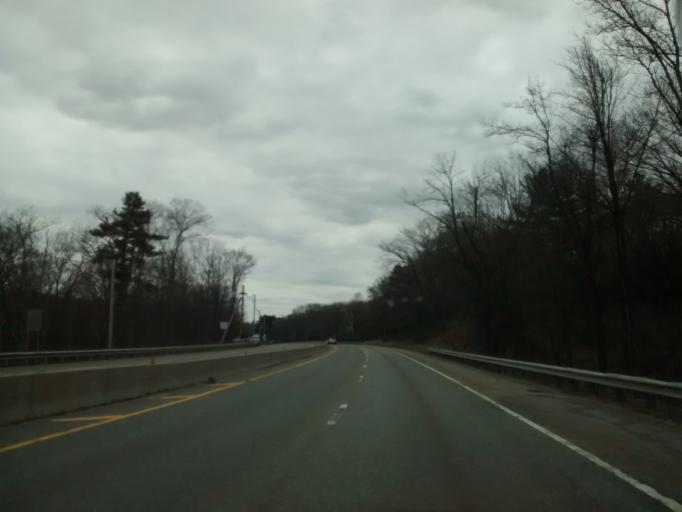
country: US
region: Massachusetts
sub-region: Worcester County
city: Charlton
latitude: 42.1469
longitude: -71.9371
